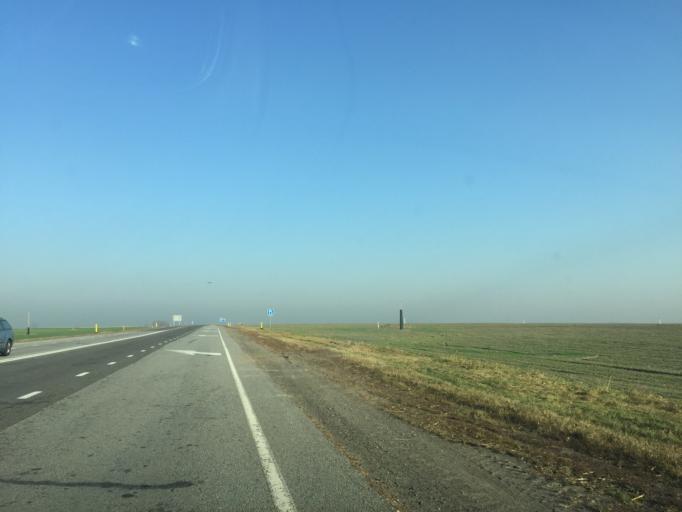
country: BY
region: Gomel
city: Kastsyukowka
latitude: 52.4925
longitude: 30.8184
